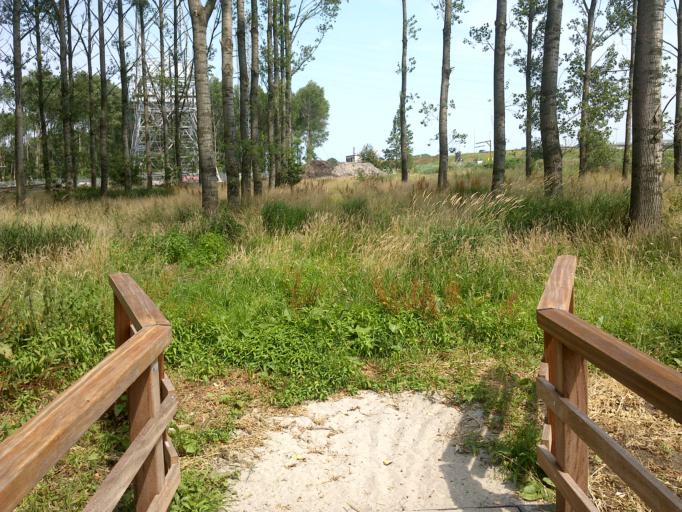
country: NL
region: South Holland
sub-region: Gemeente Leiderdorp
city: Leiderdorp
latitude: 52.1645
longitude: 4.5527
